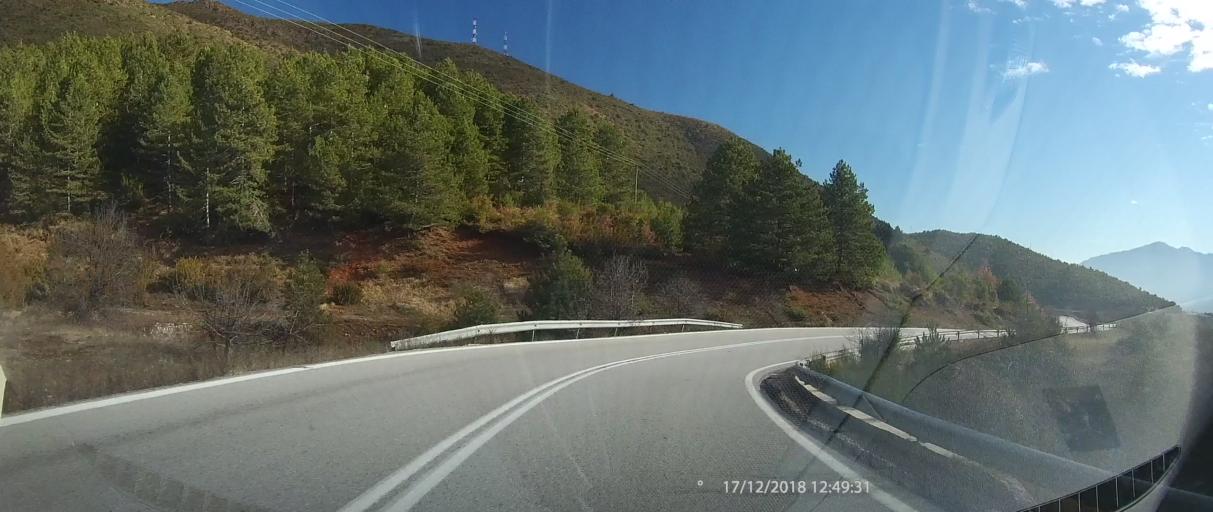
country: GR
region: Thessaly
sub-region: Trikala
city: Kastraki
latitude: 39.7784
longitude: 21.4465
